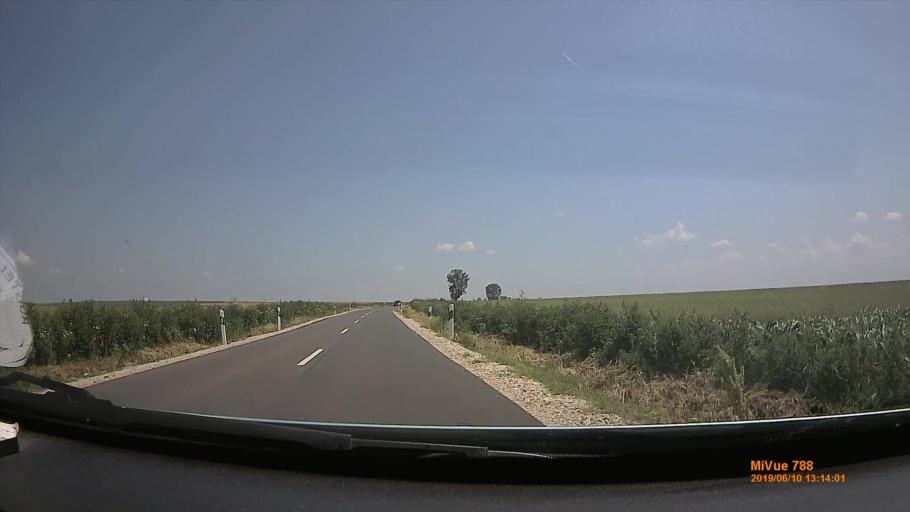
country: HU
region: Borsod-Abauj-Zemplen
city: Hernadnemeti
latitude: 48.0583
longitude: 21.0149
